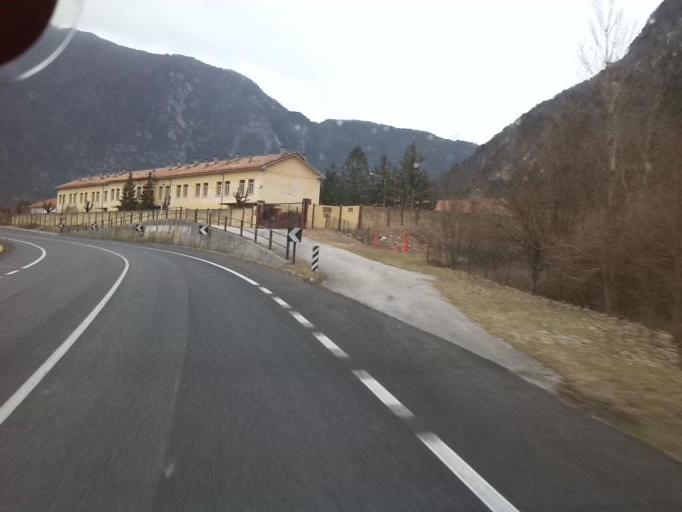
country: IT
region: Friuli Venezia Giulia
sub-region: Provincia di Udine
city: Amaro
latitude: 46.3765
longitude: 13.1371
